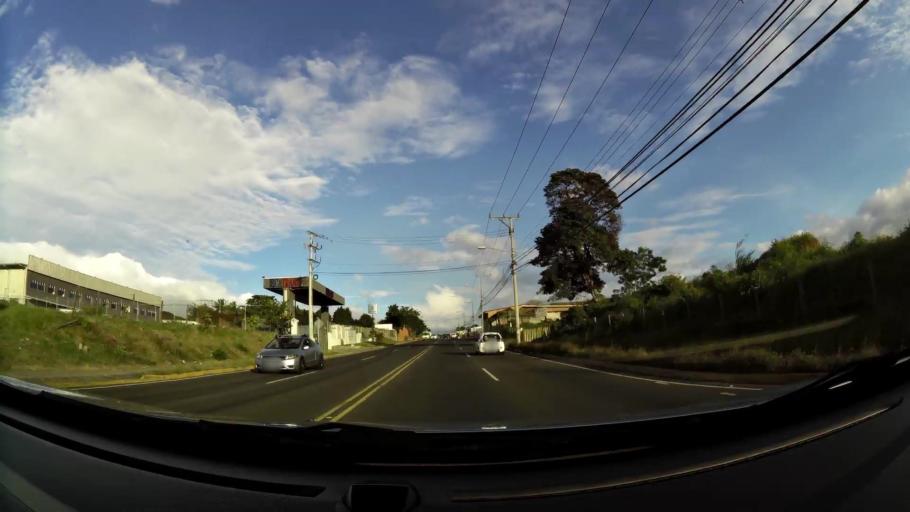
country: CR
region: Heredia
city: Llorente
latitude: 10.0026
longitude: -84.1633
